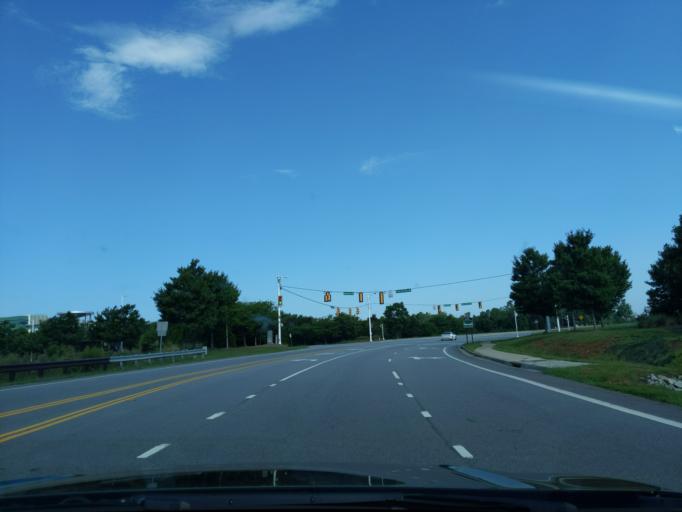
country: US
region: South Carolina
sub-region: Greenville County
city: Mauldin
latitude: 34.8182
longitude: -82.3162
